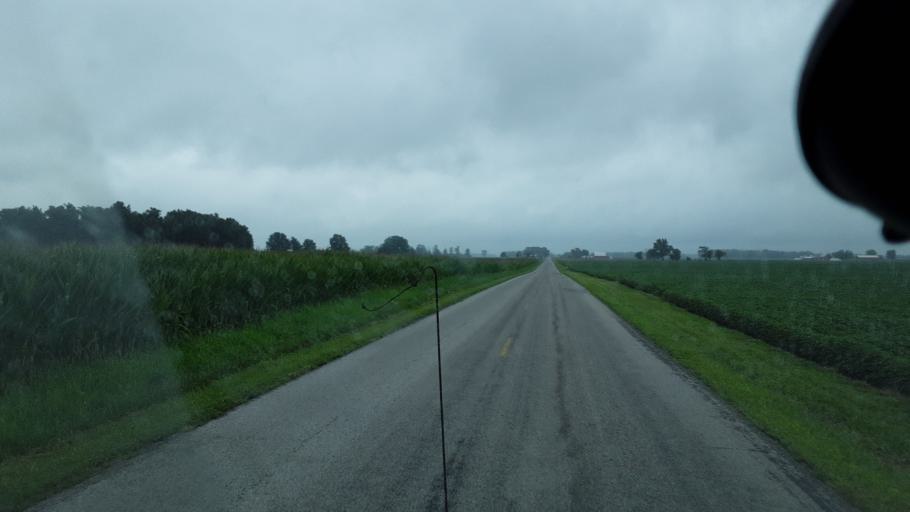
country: US
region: Indiana
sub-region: Wells County
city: Ossian
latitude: 40.8857
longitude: -85.1092
